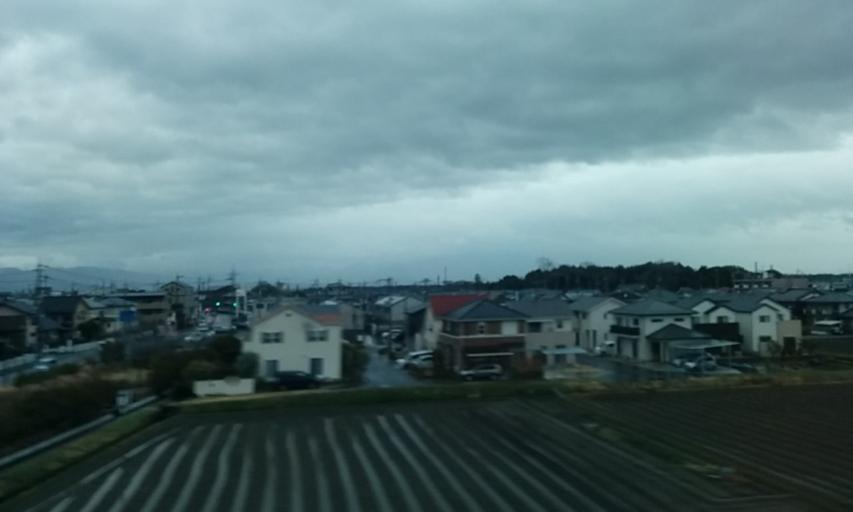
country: JP
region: Shiga Prefecture
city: Moriyama
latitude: 35.0566
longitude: 136.0170
